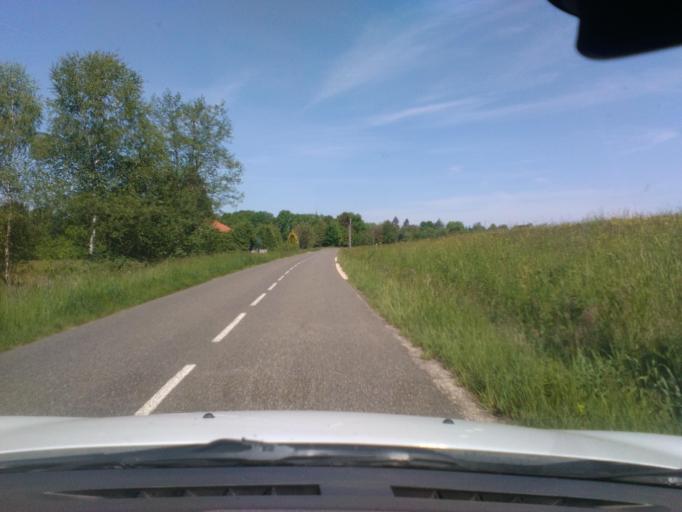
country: FR
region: Lorraine
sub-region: Departement des Vosges
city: Jeanmenil
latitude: 48.2904
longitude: 6.6928
